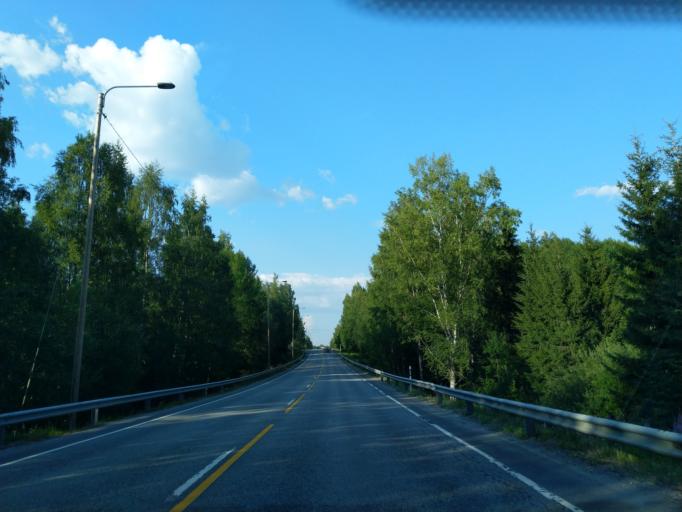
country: FI
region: Satakunta
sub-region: Pori
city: Laengelmaeki
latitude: 61.7573
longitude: 22.1338
